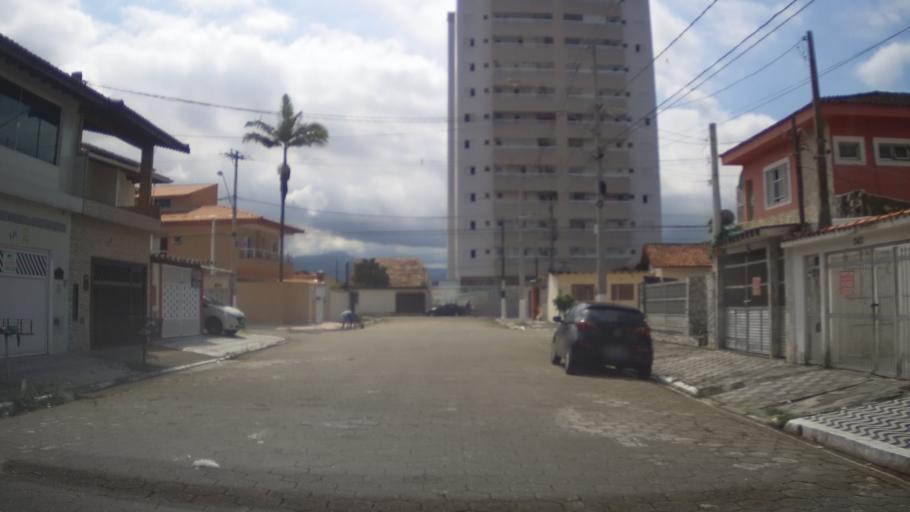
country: BR
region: Sao Paulo
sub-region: Praia Grande
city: Praia Grande
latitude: -24.0179
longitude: -46.4504
